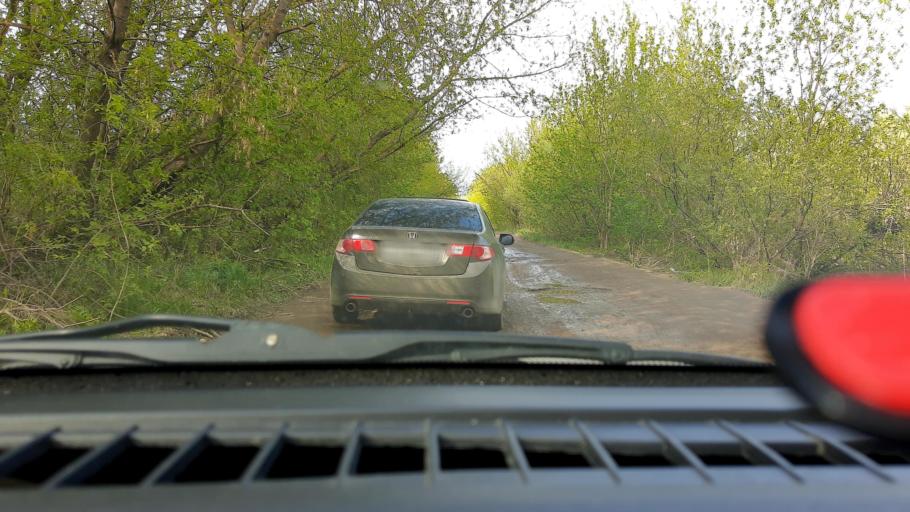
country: RU
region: Nizjnij Novgorod
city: Neklyudovo
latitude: 56.3926
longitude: 43.8454
